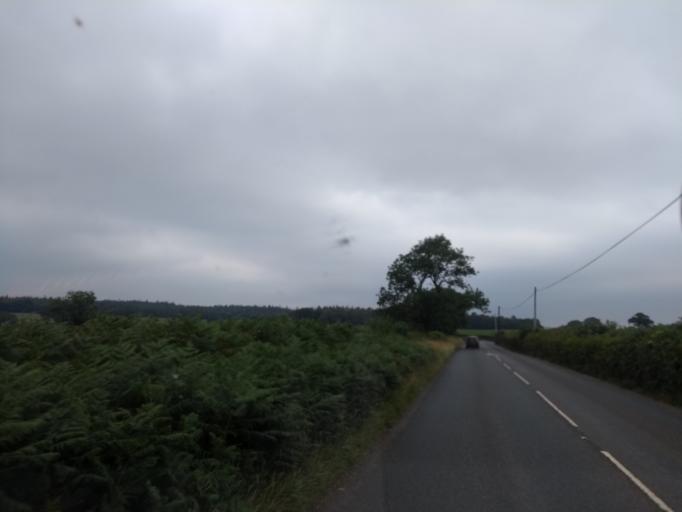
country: GB
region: England
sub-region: Somerset
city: Chard
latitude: 50.8953
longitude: -3.0822
